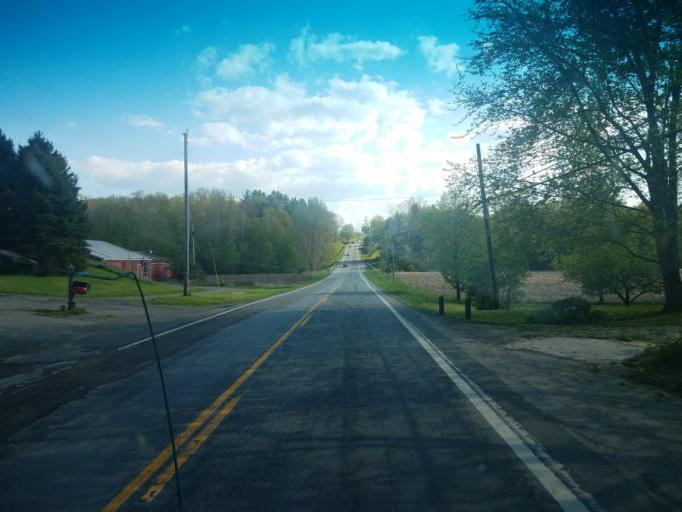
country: US
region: Ohio
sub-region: Wayne County
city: Wooster
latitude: 40.7301
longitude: -81.9403
